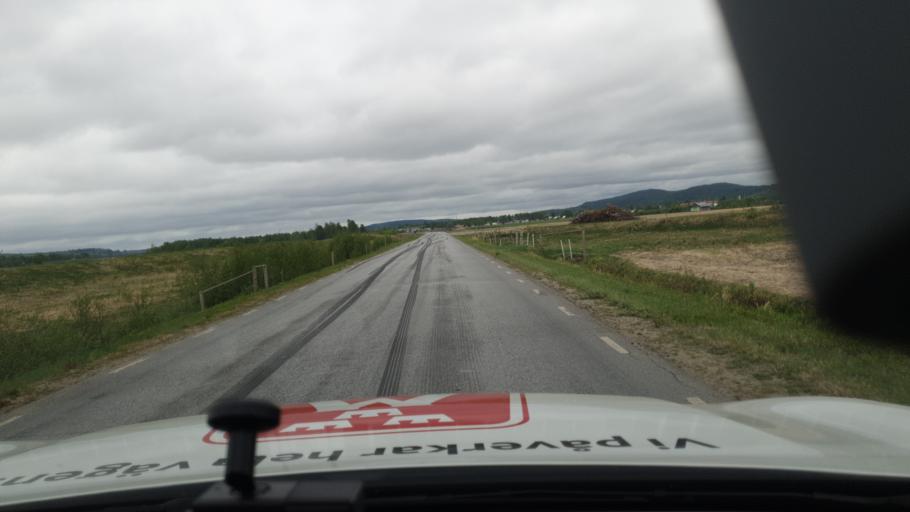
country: SE
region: Vaesterbotten
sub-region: Vannas Kommun
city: Vannasby
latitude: 63.9321
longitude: 19.8345
